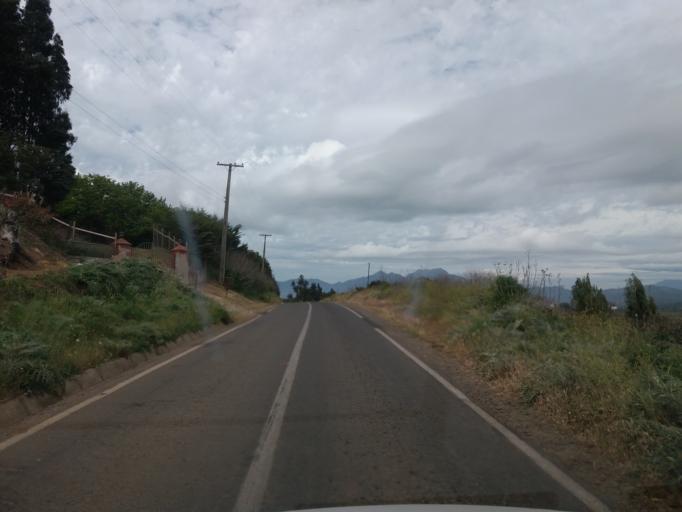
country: CL
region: Valparaiso
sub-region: Provincia de Marga Marga
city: Villa Alemana
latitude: -32.9172
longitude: -71.3725
